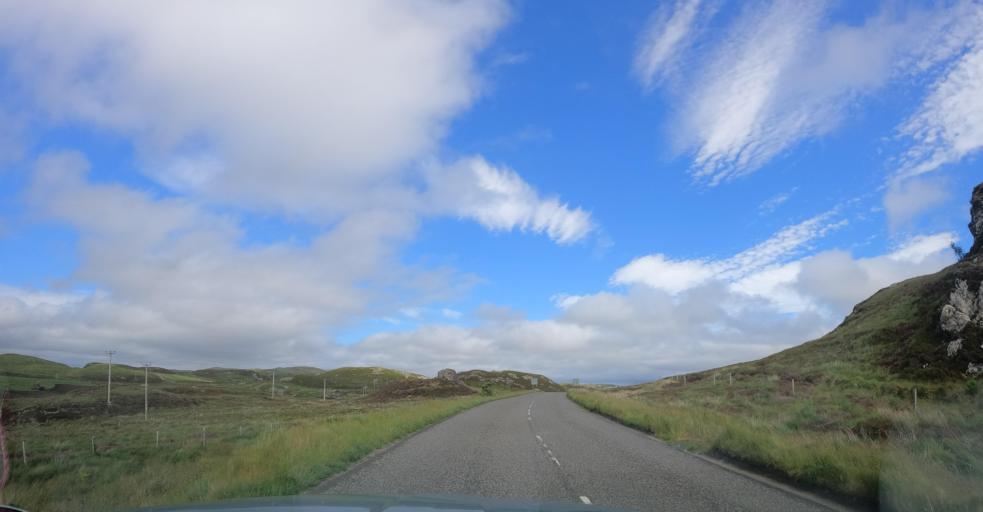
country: GB
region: Scotland
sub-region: Eilean Siar
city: Stornoway
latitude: 58.0981
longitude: -6.5745
